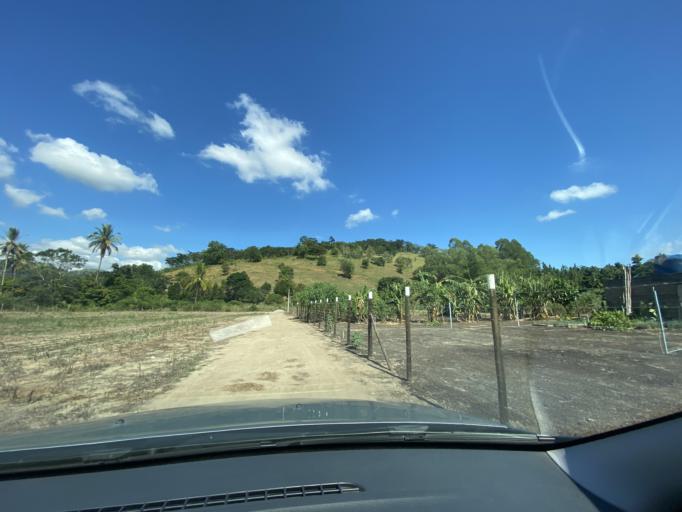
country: BR
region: Espirito Santo
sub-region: Jeronimo Monteiro
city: Jeronimo Monteiro
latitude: -20.7981
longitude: -41.4063
